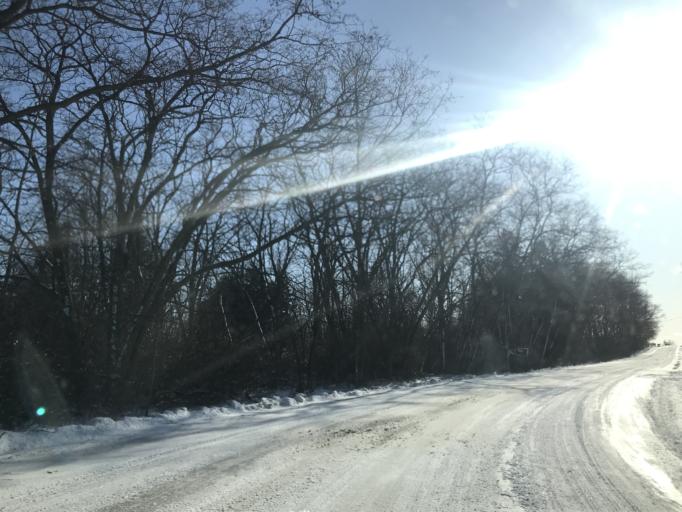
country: US
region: Wisconsin
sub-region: Door County
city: Sturgeon Bay
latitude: 44.8454
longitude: -87.5042
